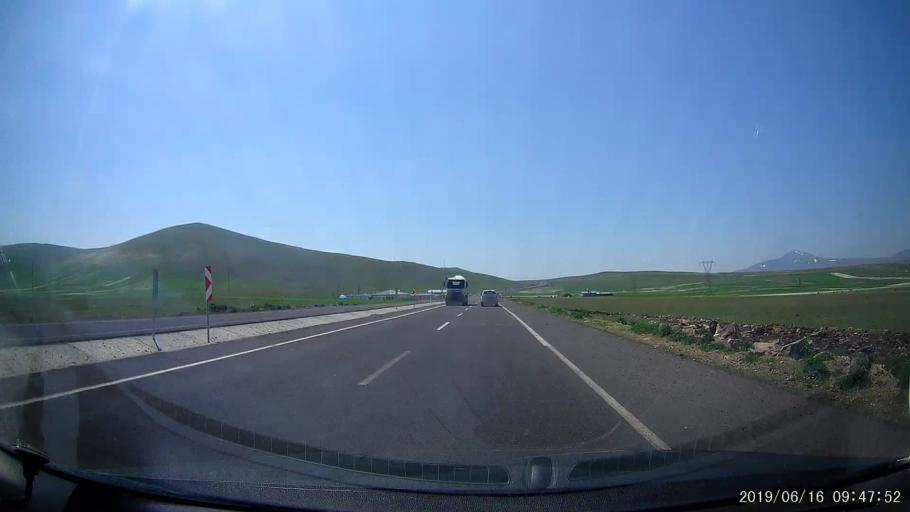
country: TR
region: Kars
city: Digor
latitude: 40.4402
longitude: 43.3486
